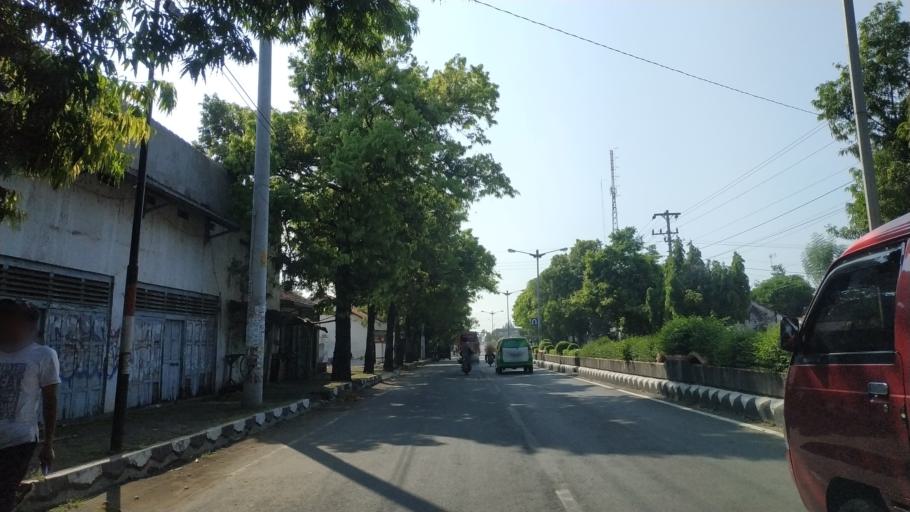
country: ID
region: Central Java
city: Petarukan
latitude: -6.8940
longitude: 109.4156
